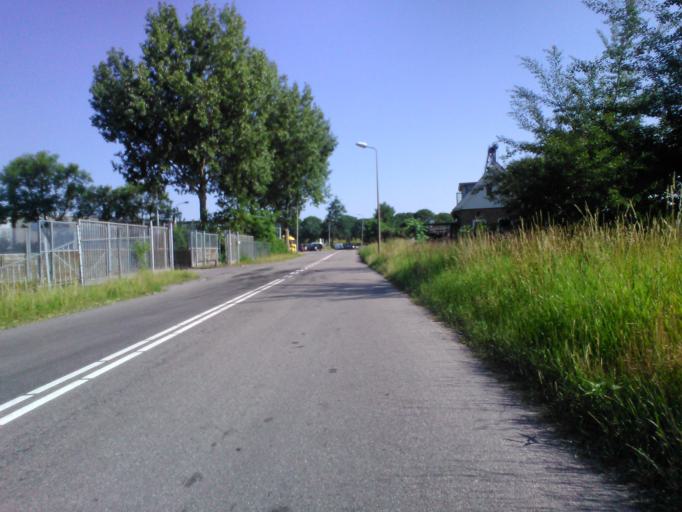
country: NL
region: South Holland
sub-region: Gemeente Alphen aan den Rijn
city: Alphen aan den Rijn
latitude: 52.1157
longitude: 4.6724
